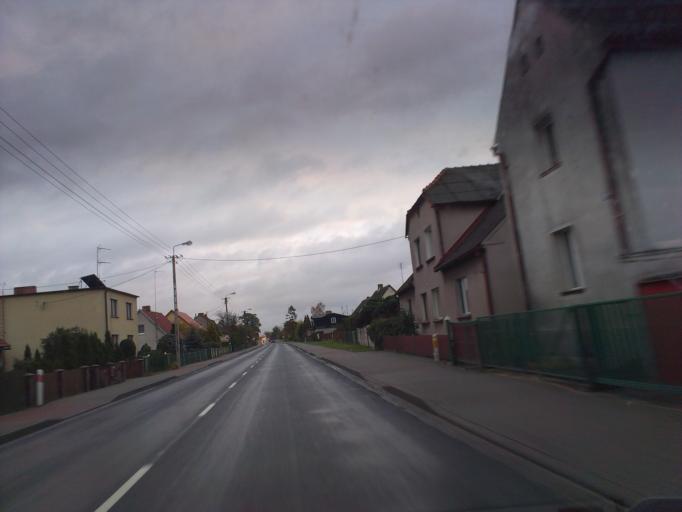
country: PL
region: Kujawsko-Pomorskie
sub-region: Powiat tucholski
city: Lubiewo
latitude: 53.5059
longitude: 17.9999
